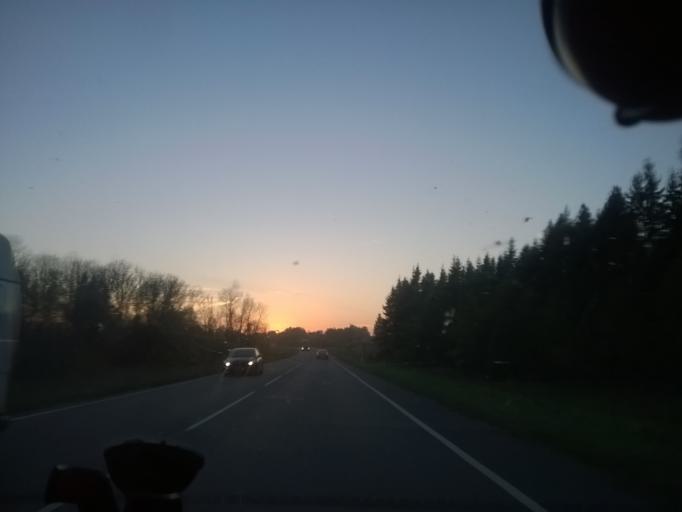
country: EE
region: Laeaene
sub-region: Ridala Parish
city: Uuemoisa
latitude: 58.9611
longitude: 23.6847
